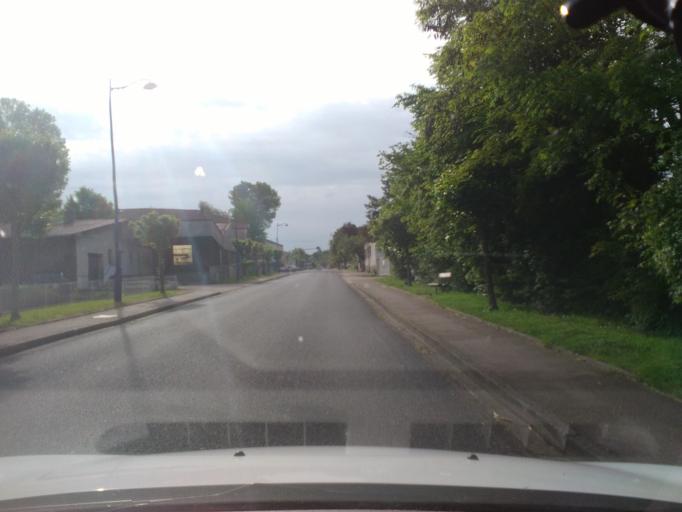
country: FR
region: Lorraine
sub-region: Departement des Vosges
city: Mirecourt
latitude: 48.3028
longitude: 6.1384
